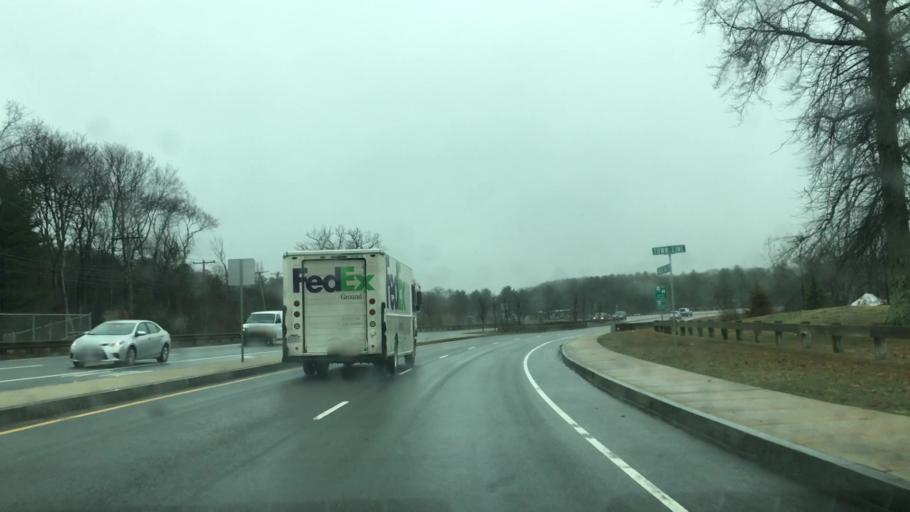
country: US
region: Massachusetts
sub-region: Middlesex County
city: Pinehurst
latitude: 42.5059
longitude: -71.2321
